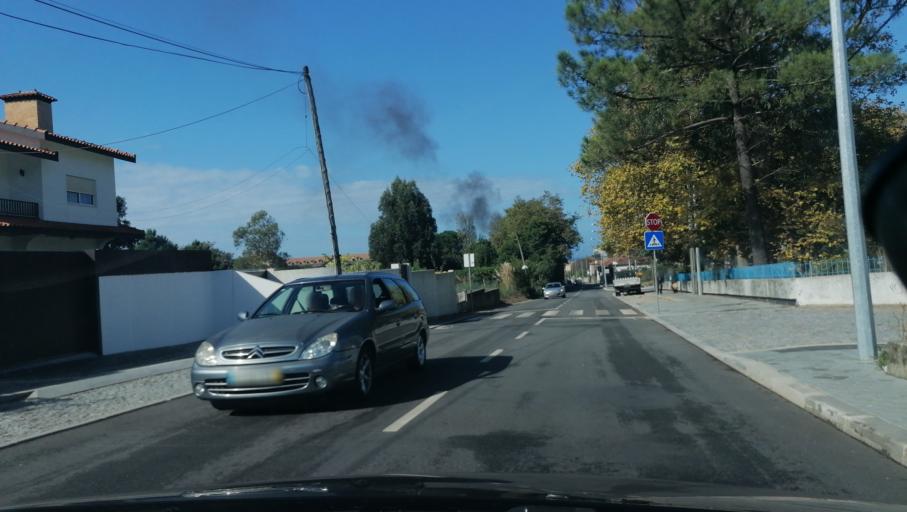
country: PT
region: Porto
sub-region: Vila Nova de Gaia
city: Arcozelo
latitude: 41.0404
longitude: -8.6394
